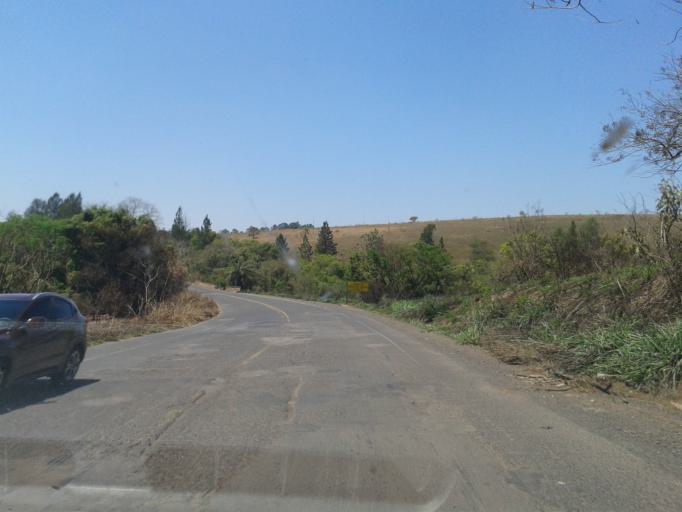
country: BR
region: Minas Gerais
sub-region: Araxa
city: Araxa
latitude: -19.4527
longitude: -47.1848
